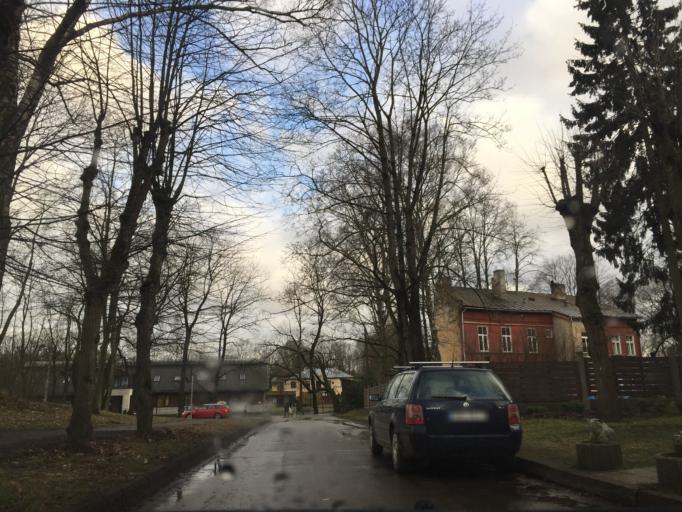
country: LV
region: Marupe
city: Marupe
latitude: 56.9417
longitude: 24.0483
